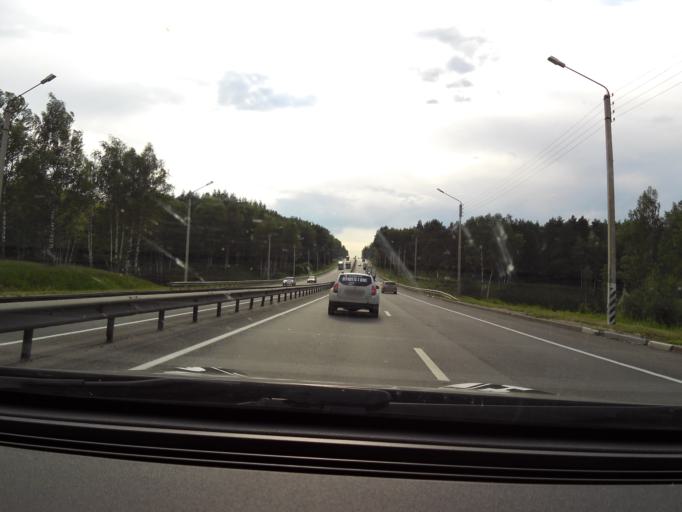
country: RU
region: Vladimir
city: Novovyazniki
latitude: 56.2198
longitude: 42.1771
